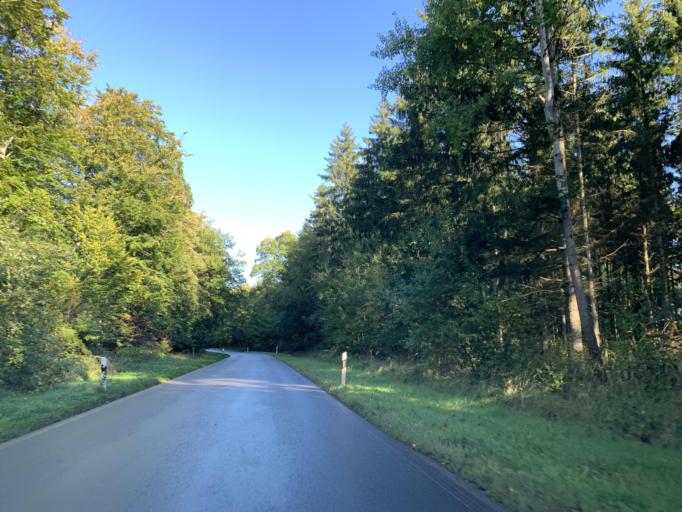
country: DE
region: Mecklenburg-Vorpommern
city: Burg Stargard
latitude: 53.5035
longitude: 13.2643
